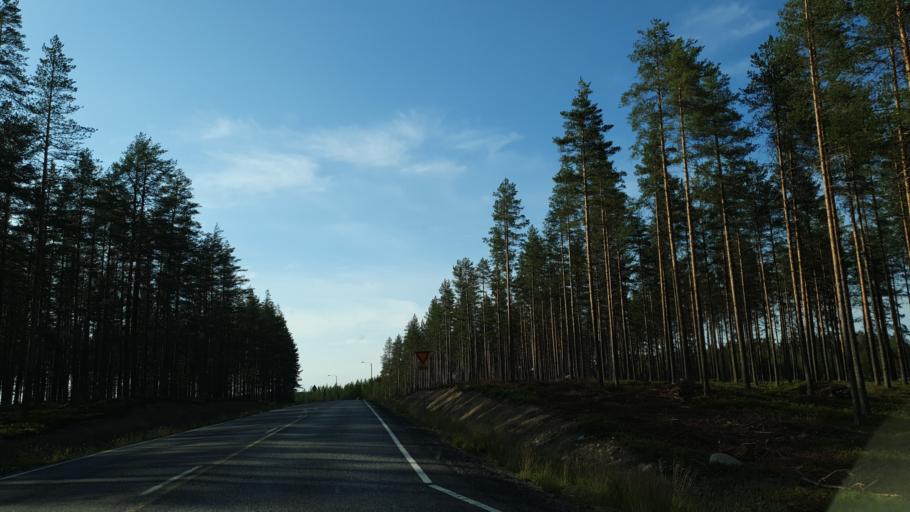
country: FI
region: Kainuu
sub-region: Kehys-Kainuu
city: Kuhmo
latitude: 64.0970
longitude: 29.4762
